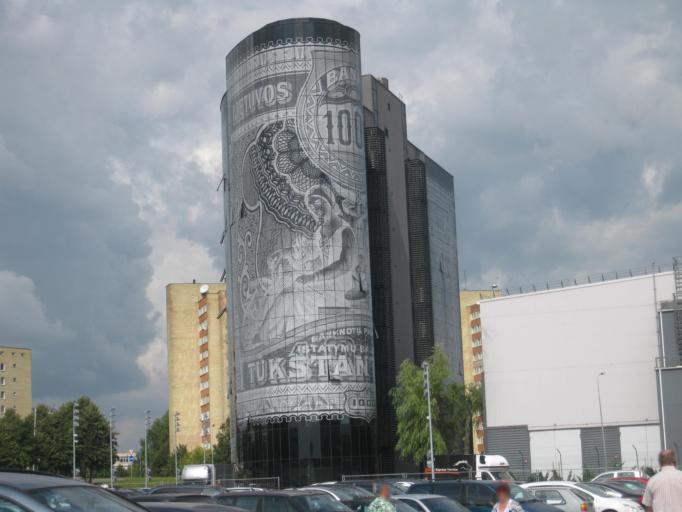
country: LT
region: Kauno apskritis
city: Dainava (Kaunas)
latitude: 54.9172
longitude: 23.9867
